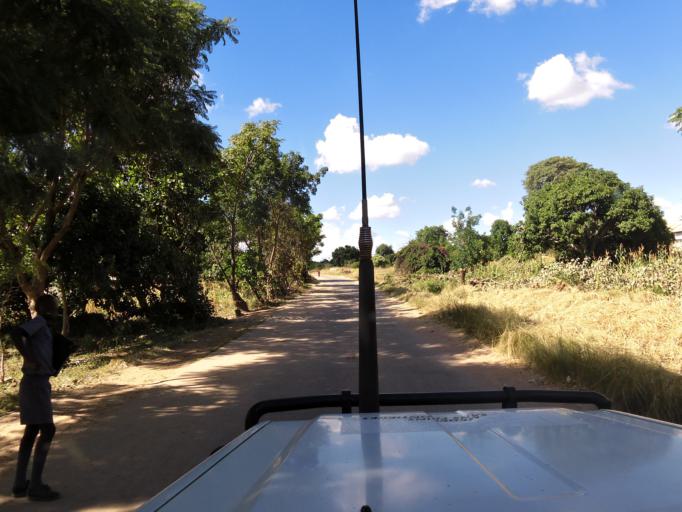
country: ZW
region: Harare
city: Epworth
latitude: -17.8750
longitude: 31.1276
